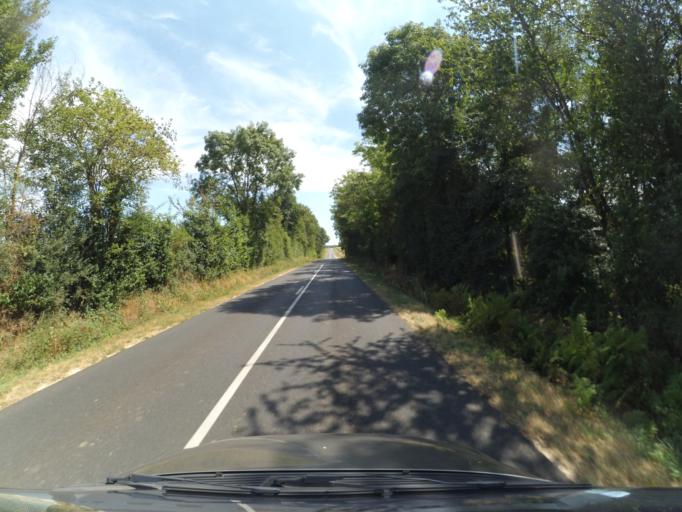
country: FR
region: Poitou-Charentes
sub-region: Departement de la Vienne
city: Saint-Maurice-la-Clouere
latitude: 46.3598
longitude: 0.4362
